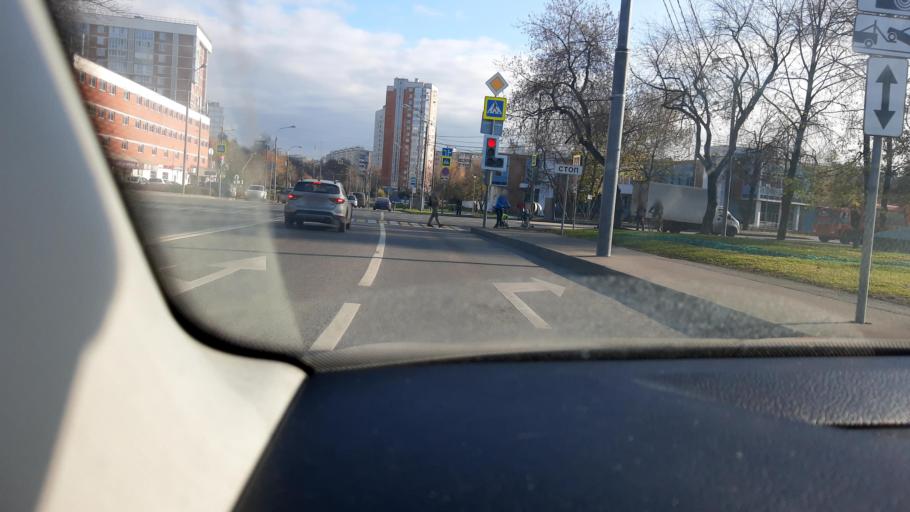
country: RU
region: Moscow
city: Orekhovo-Borisovo Severnoye
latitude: 55.6173
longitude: 37.6933
